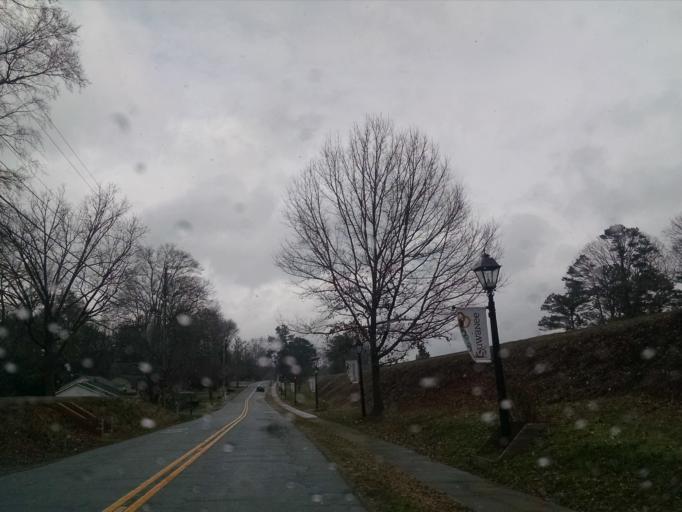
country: US
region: Georgia
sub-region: Gwinnett County
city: Suwanee
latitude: 34.0533
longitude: -84.0714
